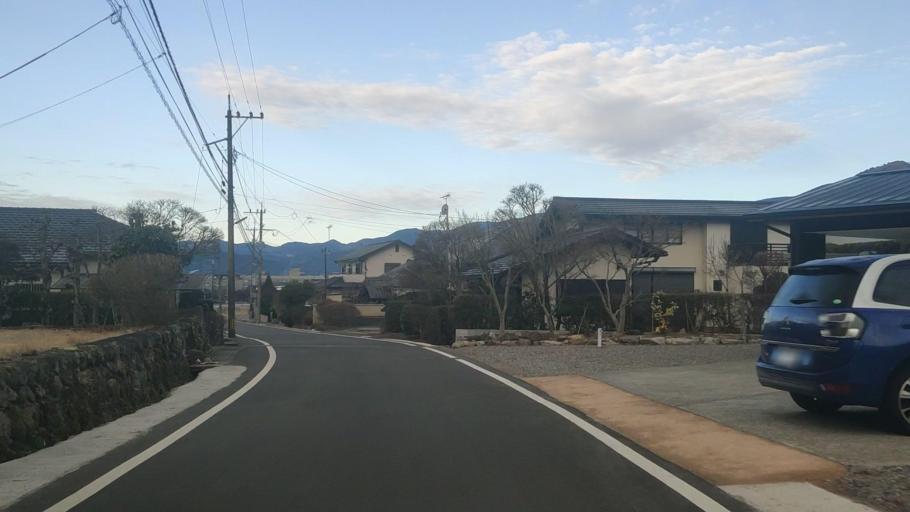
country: JP
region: Oita
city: Beppu
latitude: 33.2612
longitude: 131.3670
